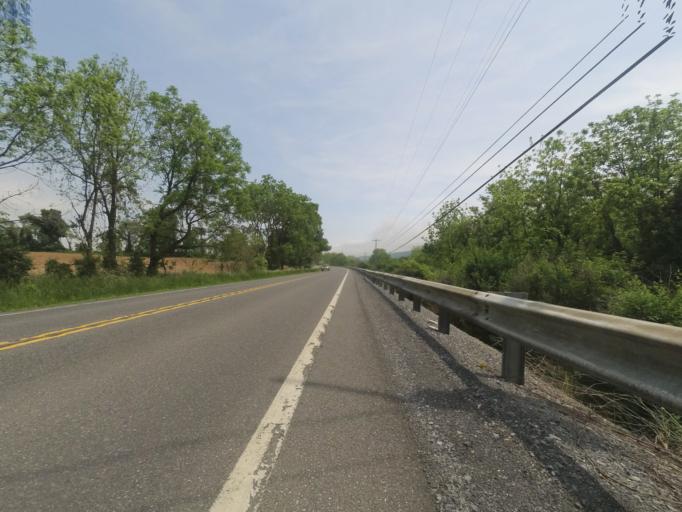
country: US
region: Pennsylvania
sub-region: Centre County
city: Stormstown
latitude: 40.7046
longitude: -77.9784
